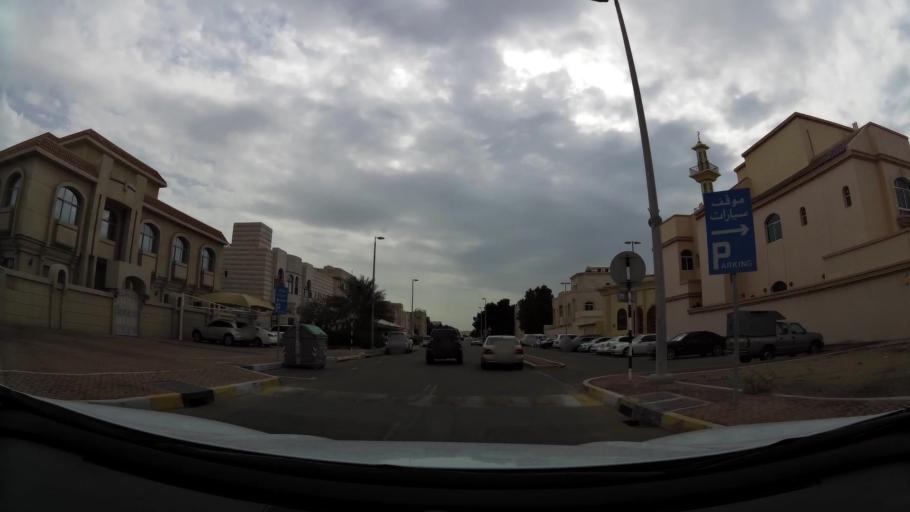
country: AE
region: Abu Dhabi
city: Abu Dhabi
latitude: 24.4296
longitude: 54.4157
